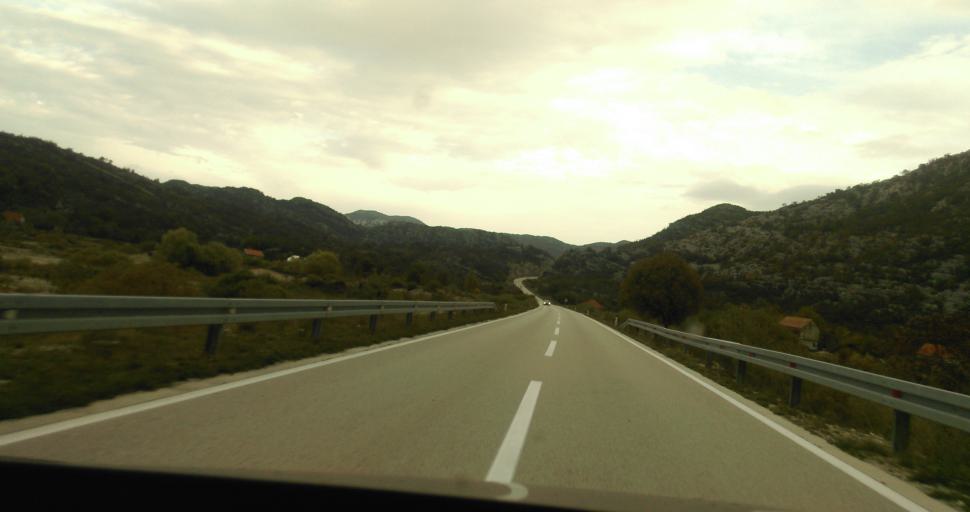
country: ME
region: Kotor
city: Risan
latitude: 42.6187
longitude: 18.6817
